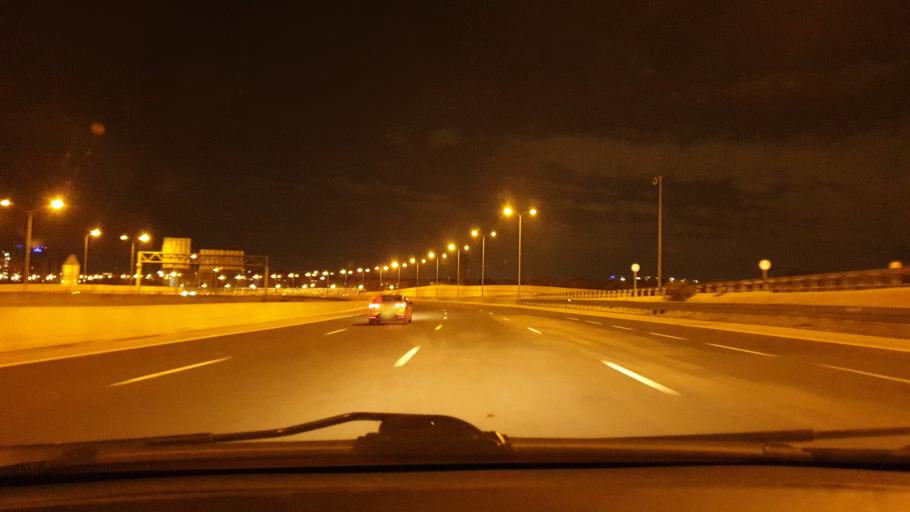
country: IL
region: Central District
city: Ness Ziona
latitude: 31.9409
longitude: 34.8153
